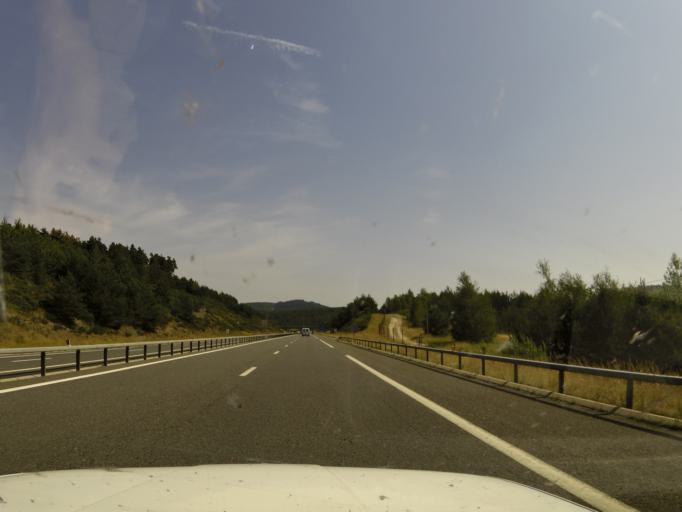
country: FR
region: Languedoc-Roussillon
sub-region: Departement de la Lozere
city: Aumont-Aubrac
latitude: 44.7585
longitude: 3.2860
